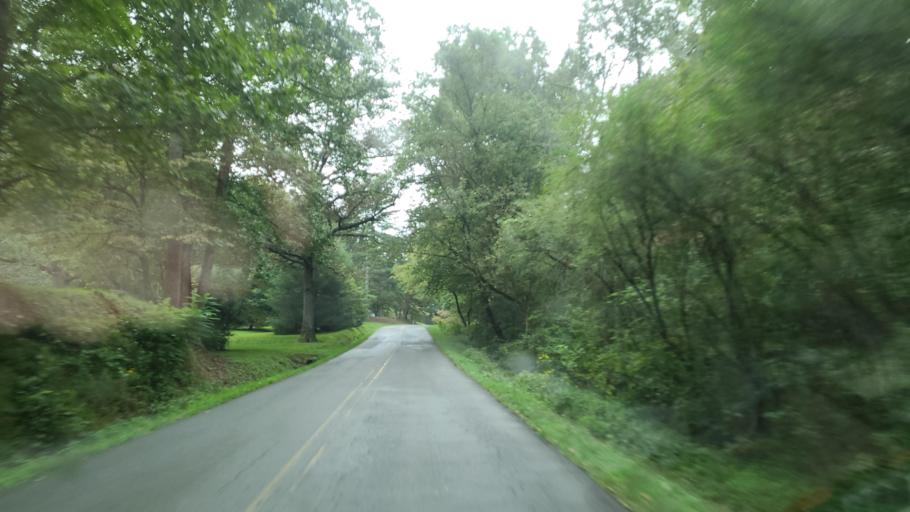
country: US
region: Georgia
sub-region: Gilmer County
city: Ellijay
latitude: 34.7570
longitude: -84.5294
